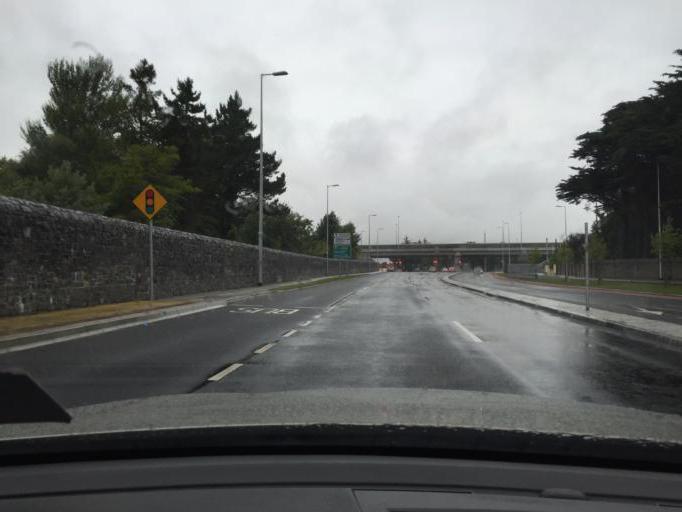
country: IE
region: Leinster
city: Clondalkin
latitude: 53.3110
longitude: -6.3893
